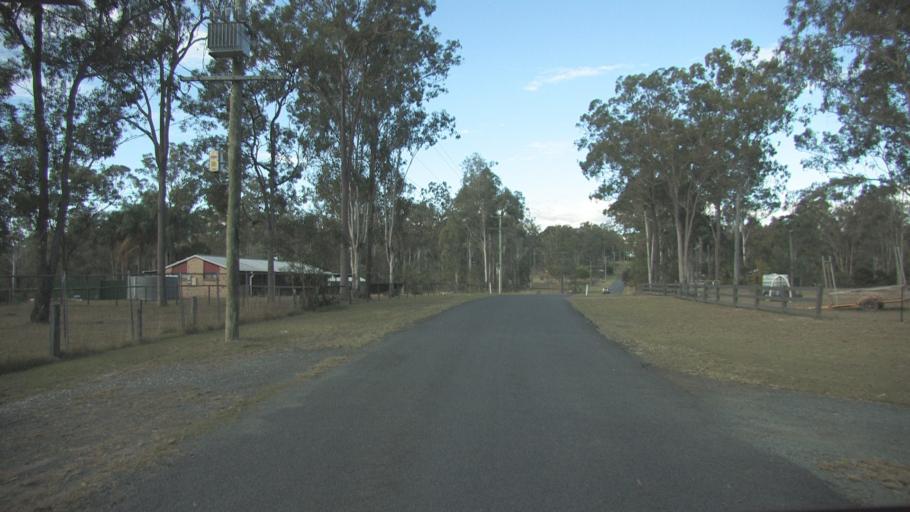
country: AU
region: Queensland
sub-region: Logan
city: North Maclean
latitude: -27.8181
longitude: 153.0476
